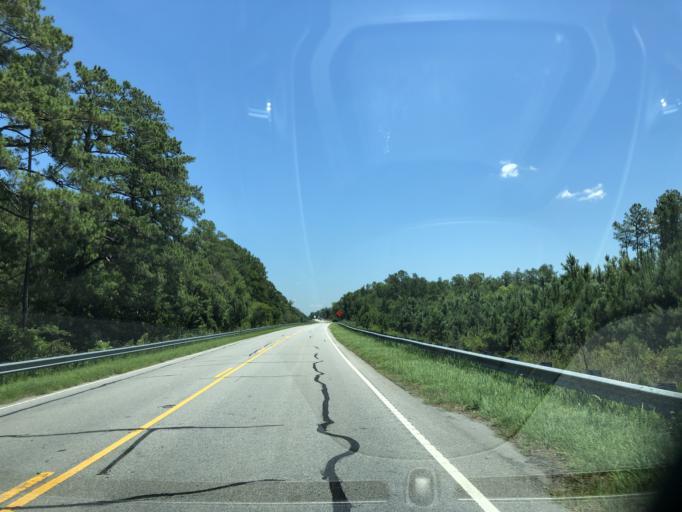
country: US
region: South Carolina
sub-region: Orangeburg County
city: Branchville
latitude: 33.2387
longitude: -80.8643
